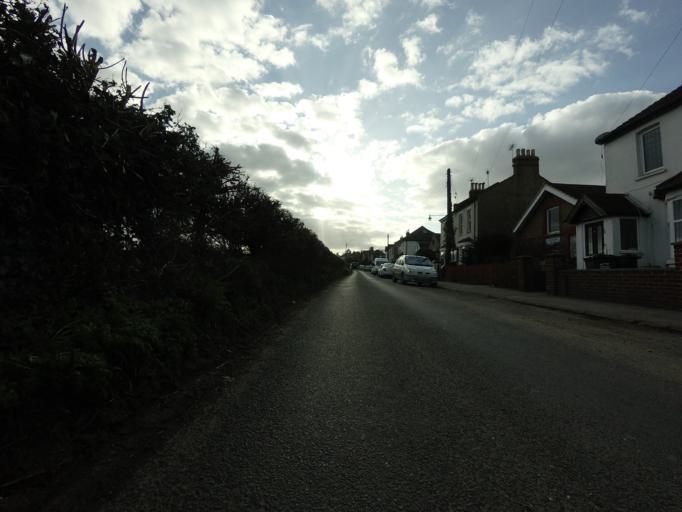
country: GB
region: England
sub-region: Kent
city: Dartford
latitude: 51.4226
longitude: 0.2302
